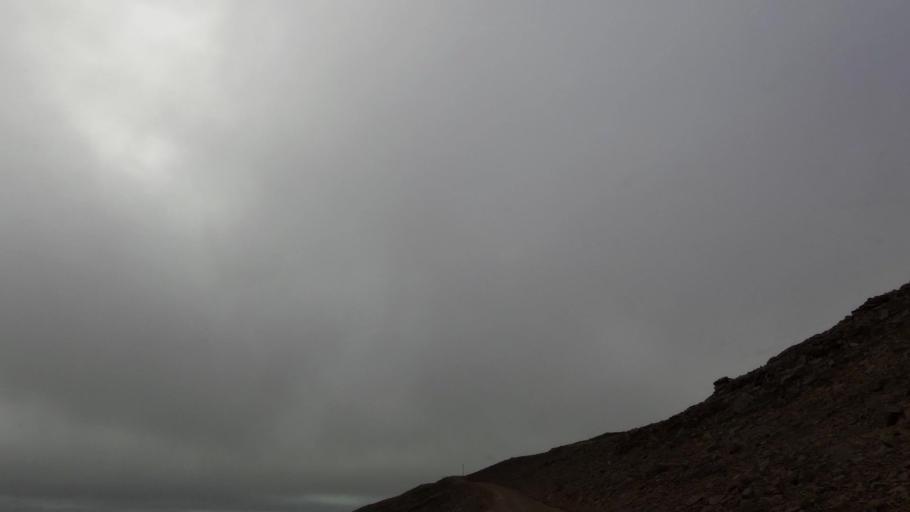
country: IS
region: West
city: Olafsvik
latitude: 65.5275
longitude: -24.4262
